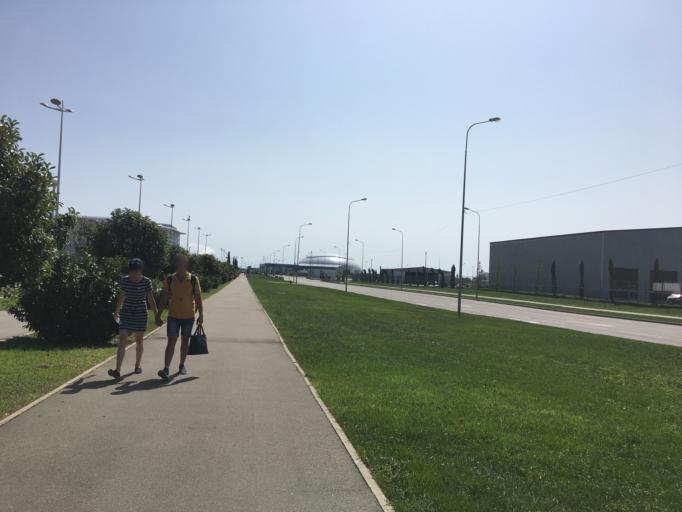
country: RU
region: Krasnodarskiy
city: Adler
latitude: 43.4160
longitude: 39.9475
